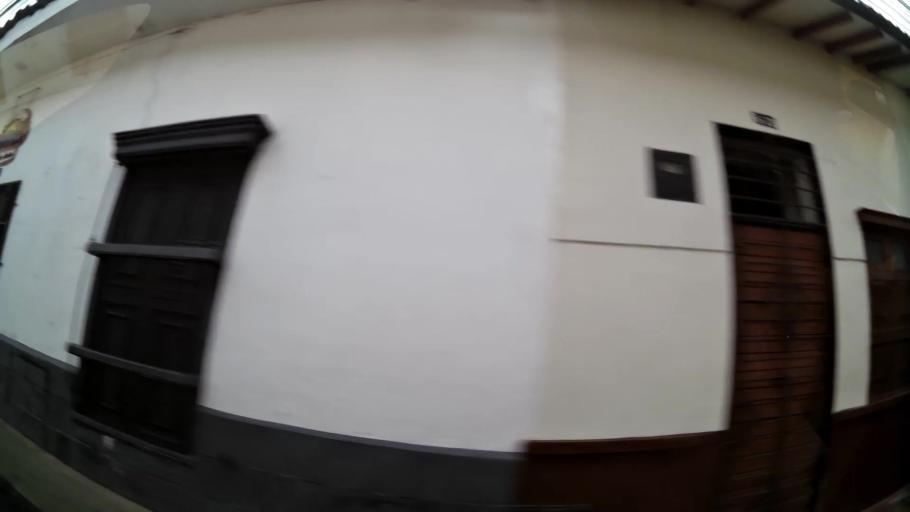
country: CO
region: Valle del Cauca
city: Cali
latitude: 3.4477
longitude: -76.5379
